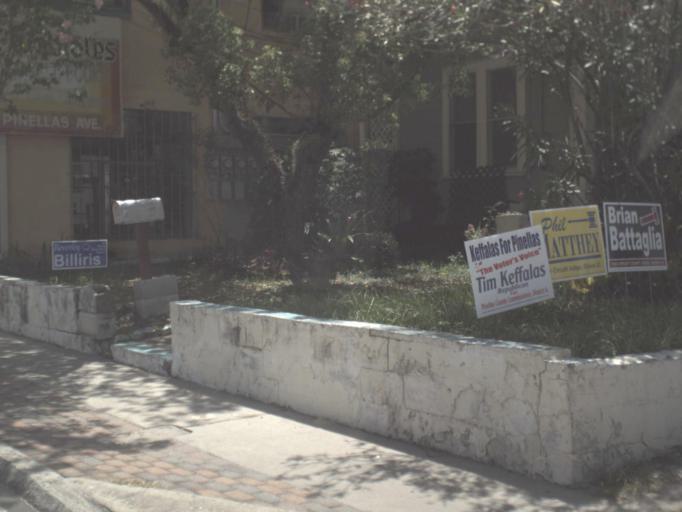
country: US
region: Florida
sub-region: Pinellas County
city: Tarpon Springs
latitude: 28.1487
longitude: -82.7568
